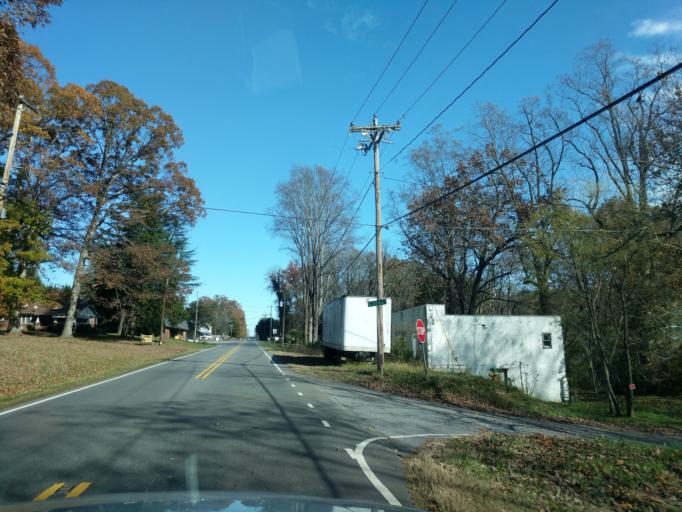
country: US
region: North Carolina
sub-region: Iredell County
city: Statesville
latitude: 35.7790
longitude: -80.9271
